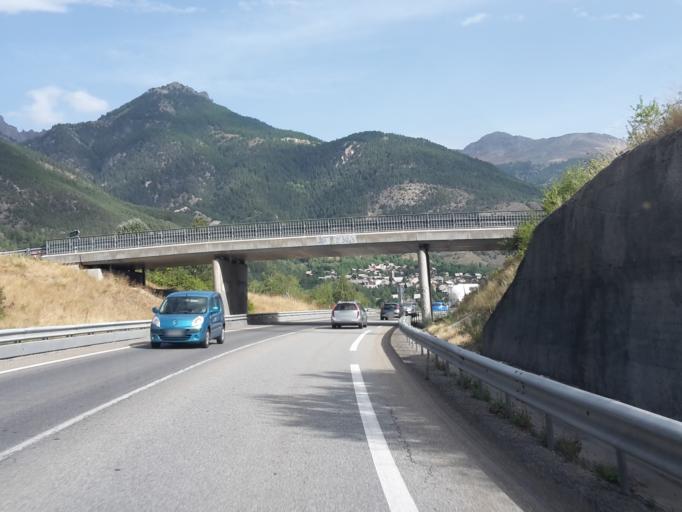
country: FR
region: Provence-Alpes-Cote d'Azur
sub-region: Departement des Hautes-Alpes
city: Saint-Martin-de-Queyrieres
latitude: 44.8430
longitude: 6.5828
